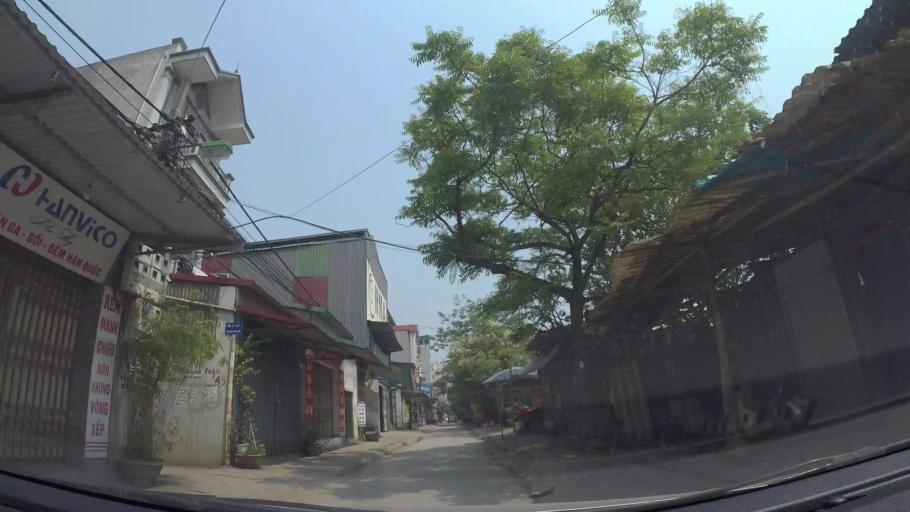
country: VN
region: Ha Noi
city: Ha Dong
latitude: 20.9903
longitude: 105.7706
